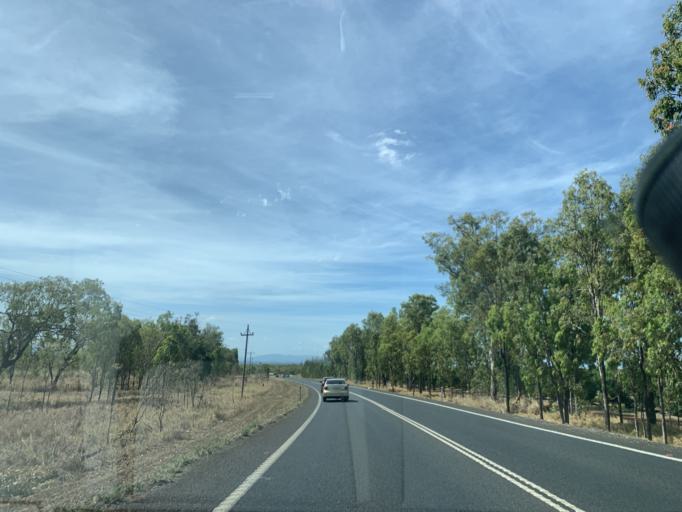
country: AU
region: Queensland
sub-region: Tablelands
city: Mareeba
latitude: -17.0998
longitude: 145.4369
